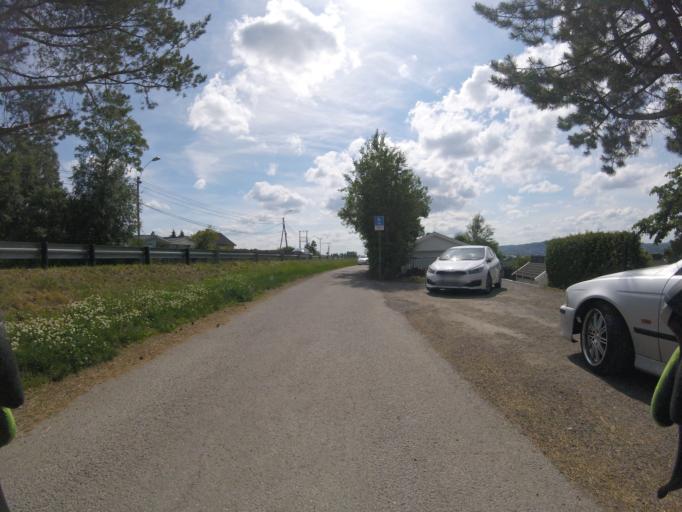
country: NO
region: Akershus
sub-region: Skedsmo
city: Lillestrom
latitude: 59.9822
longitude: 11.0514
